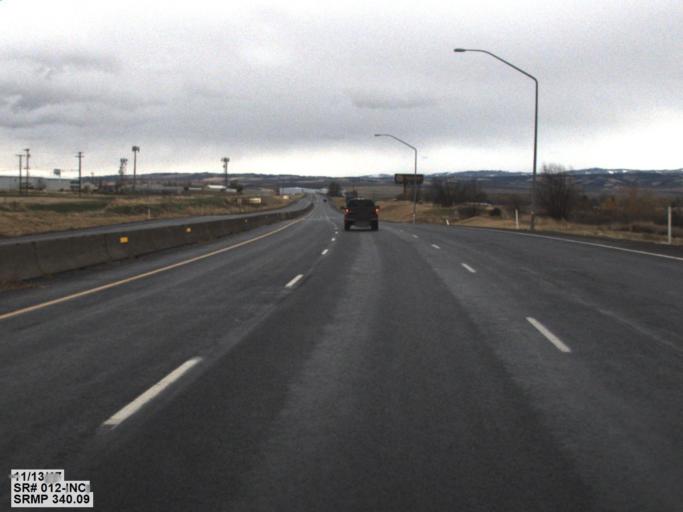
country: US
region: Washington
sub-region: Walla Walla County
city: Walla Walla East
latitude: 46.0844
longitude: -118.2768
